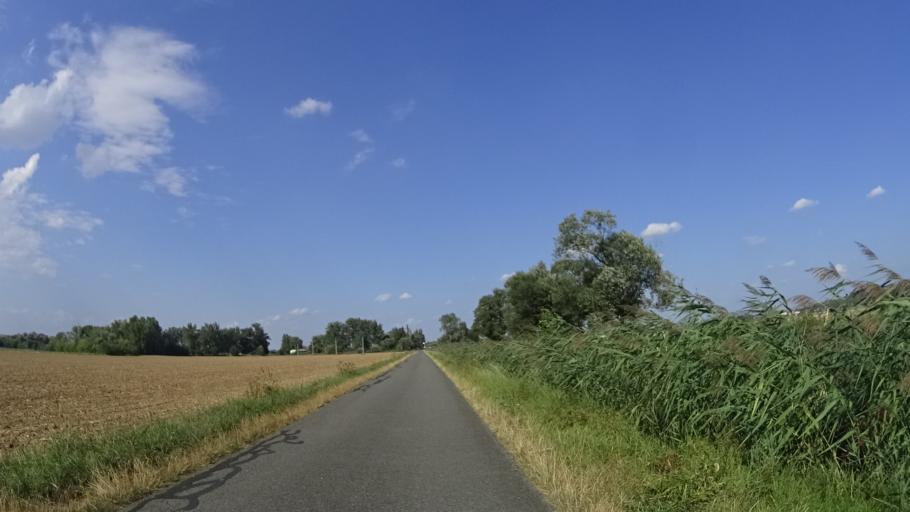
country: CZ
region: Zlin
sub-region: Okres Uherske Hradiste
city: Uherske Hradiste
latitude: 49.0812
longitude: 17.4627
